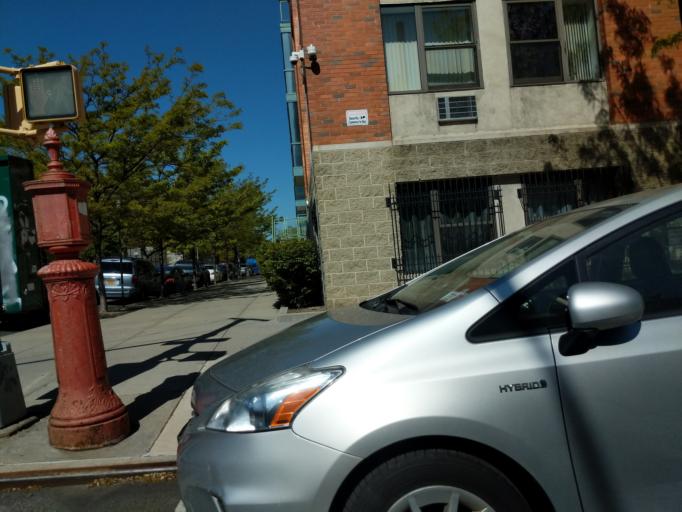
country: US
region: New York
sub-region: Kings County
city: Brooklyn
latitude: 40.6753
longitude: -73.9333
